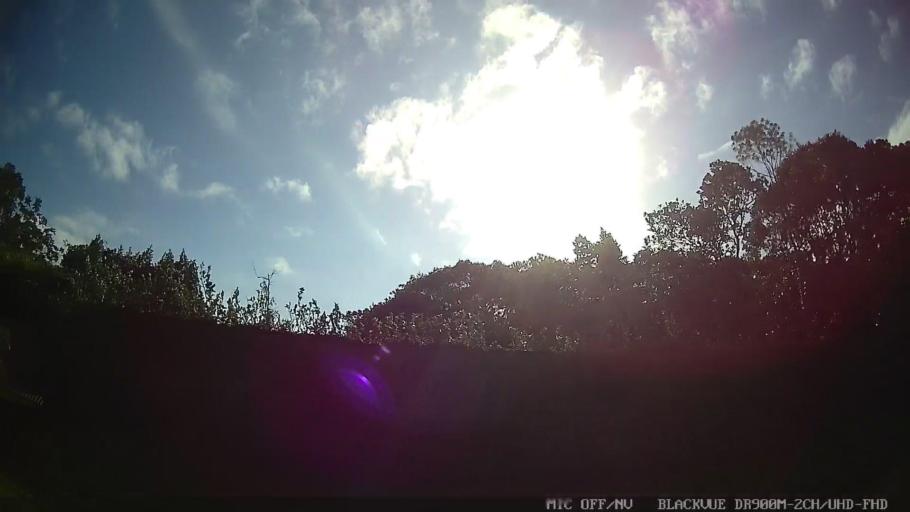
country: BR
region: Sao Paulo
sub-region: Itanhaem
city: Itanhaem
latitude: -24.2138
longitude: -46.8819
